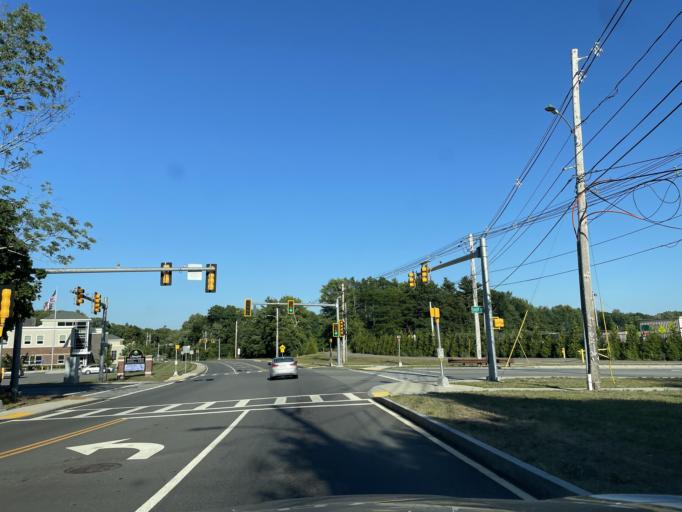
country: US
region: Massachusetts
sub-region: Bristol County
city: Mansfield
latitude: 42.0326
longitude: -71.1976
